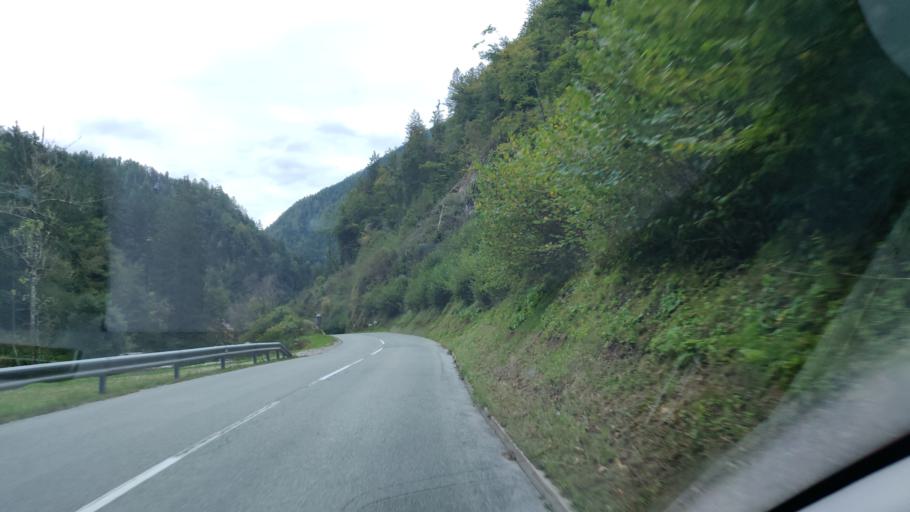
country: SI
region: Jezersko
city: Zgornje Jezersko
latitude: 46.3633
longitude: 14.4699
